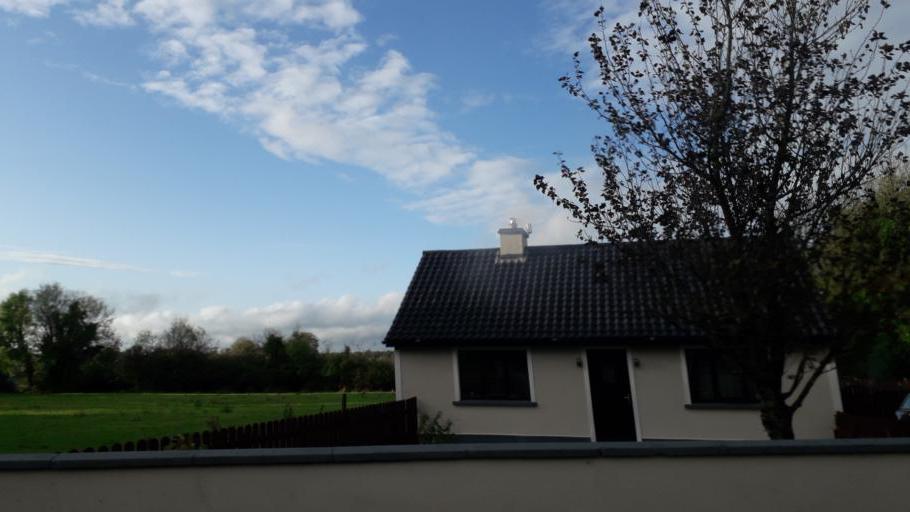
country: IE
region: Connaught
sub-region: Roscommon
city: Roscommon
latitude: 53.7729
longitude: -8.1446
